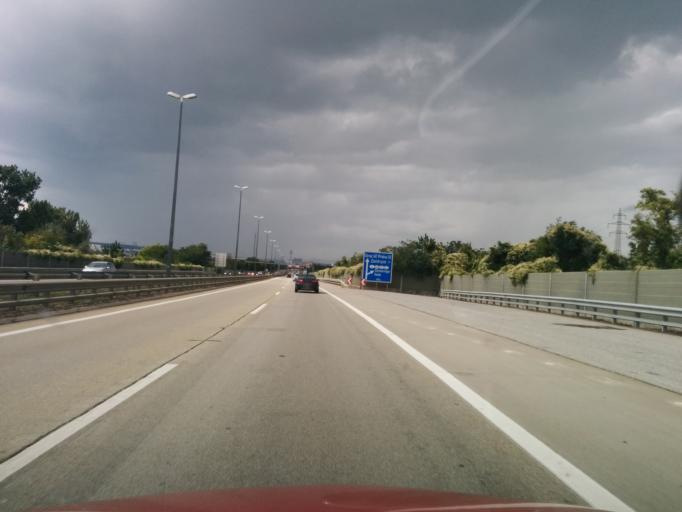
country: AT
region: Lower Austria
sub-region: Politischer Bezirk Wien-Umgebung
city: Schwechat
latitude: 48.1648
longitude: 16.4718
